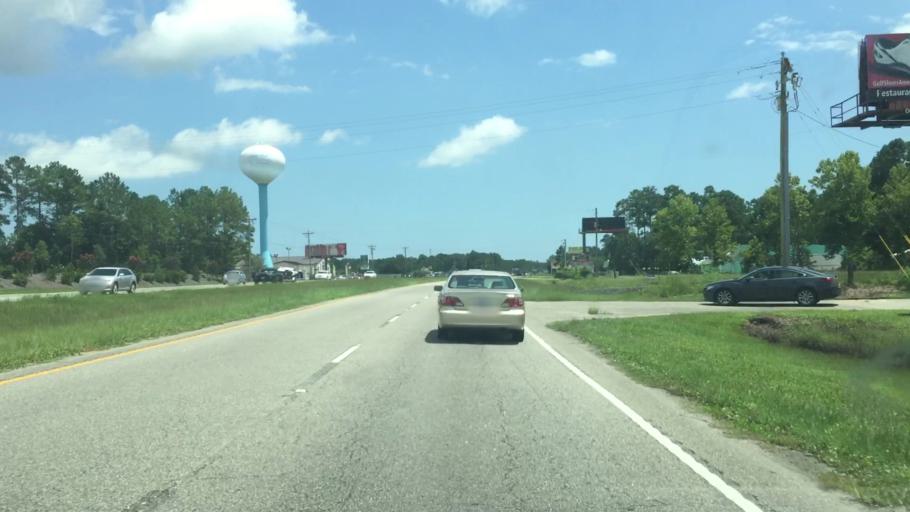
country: US
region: South Carolina
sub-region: Horry County
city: North Myrtle Beach
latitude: 33.9044
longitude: -78.7036
